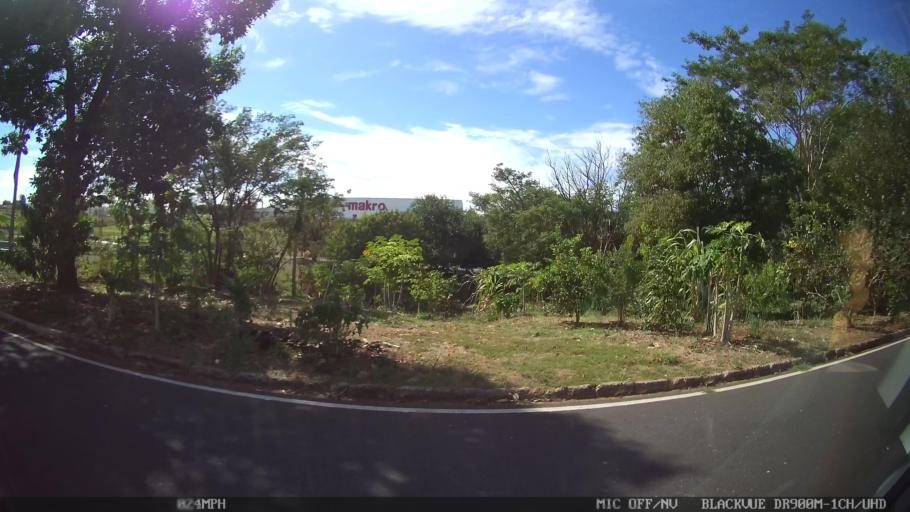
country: BR
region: Sao Paulo
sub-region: Sao Jose Do Rio Preto
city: Sao Jose do Rio Preto
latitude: -20.8397
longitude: -49.3662
